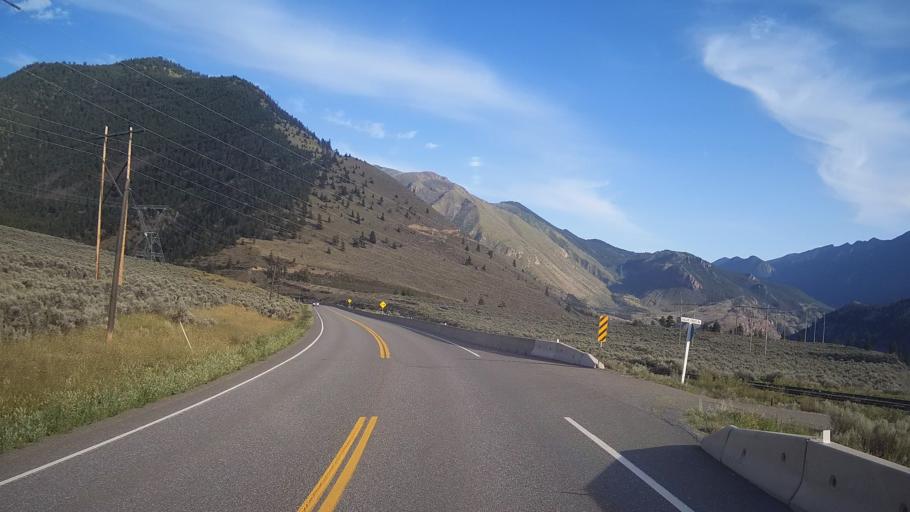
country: CA
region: British Columbia
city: Lillooet
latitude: 50.7984
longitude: -121.8436
